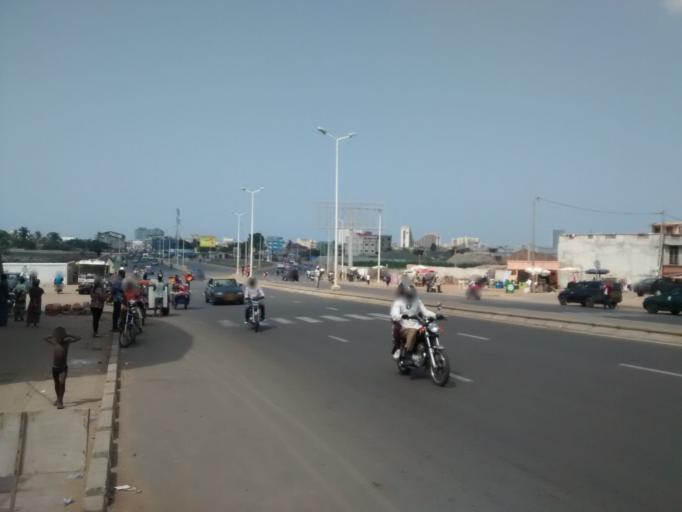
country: TG
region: Maritime
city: Lome
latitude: 6.1470
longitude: 1.2300
